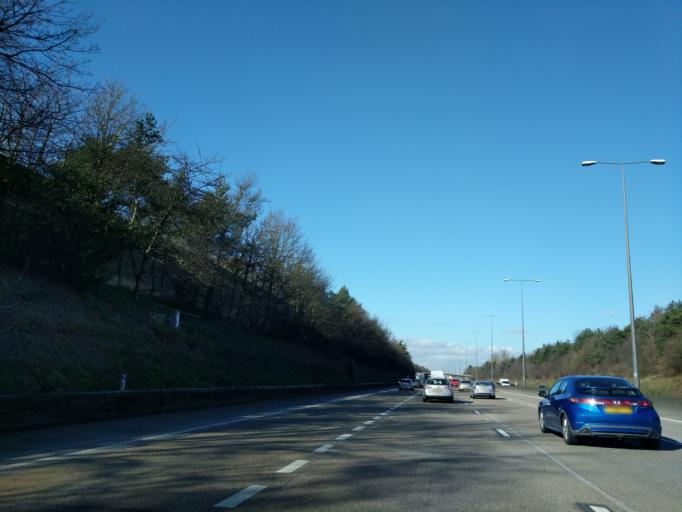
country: GB
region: England
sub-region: Surrey
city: Addlestone
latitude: 51.3618
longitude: -0.4989
